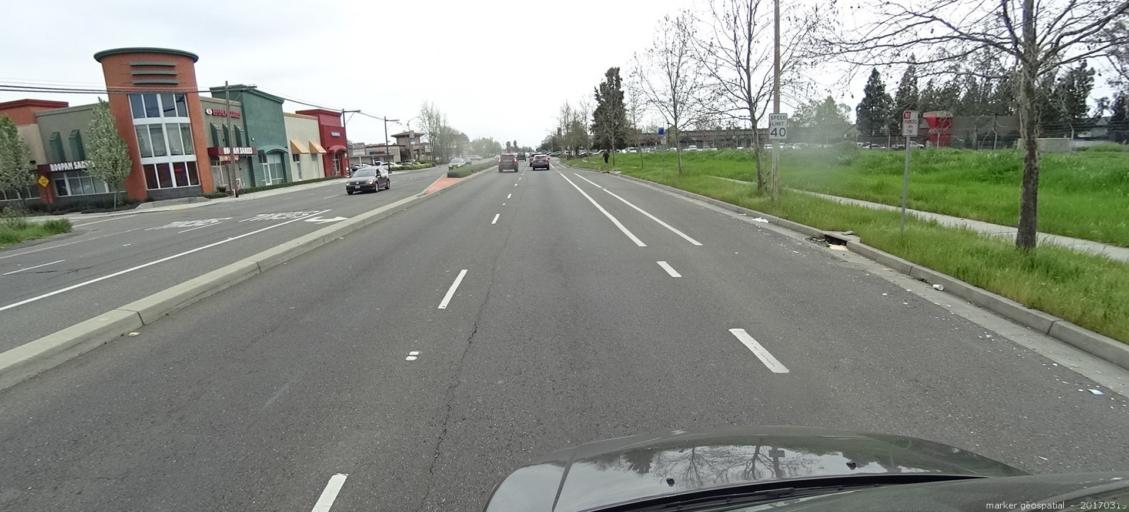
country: US
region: California
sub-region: Sacramento County
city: Florin
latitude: 38.5043
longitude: -121.4331
